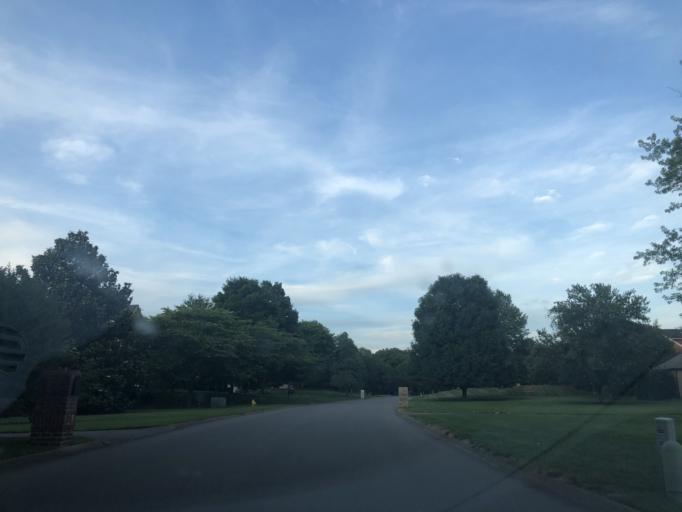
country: US
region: Tennessee
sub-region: Davidson County
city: Forest Hills
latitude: 36.0465
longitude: -86.9251
